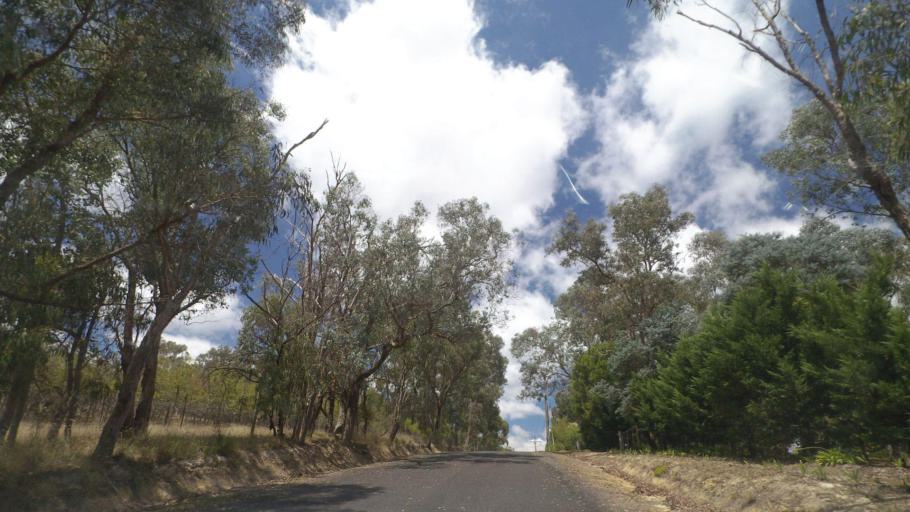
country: AU
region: Victoria
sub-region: Manningham
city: Warrandyte
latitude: -37.7480
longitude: 145.2586
